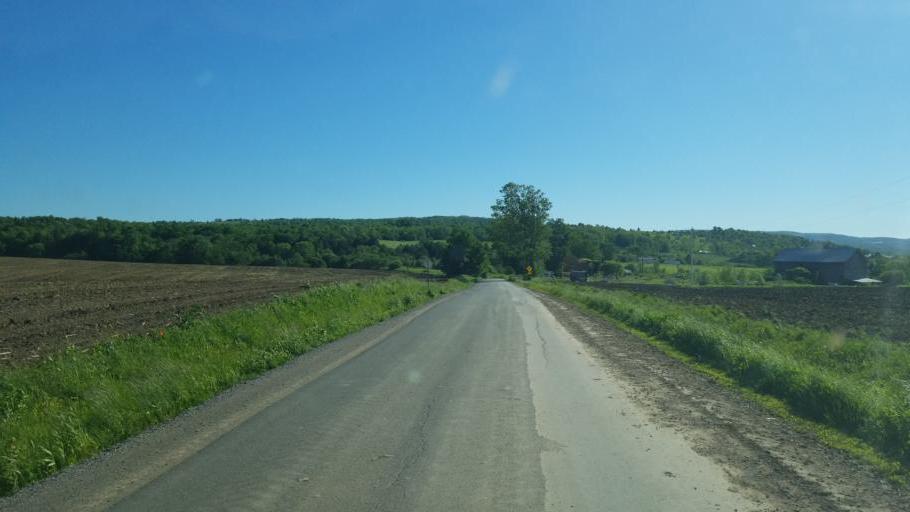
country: US
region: New York
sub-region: Montgomery County
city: Saint Johnsville
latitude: 42.9824
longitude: -74.7713
